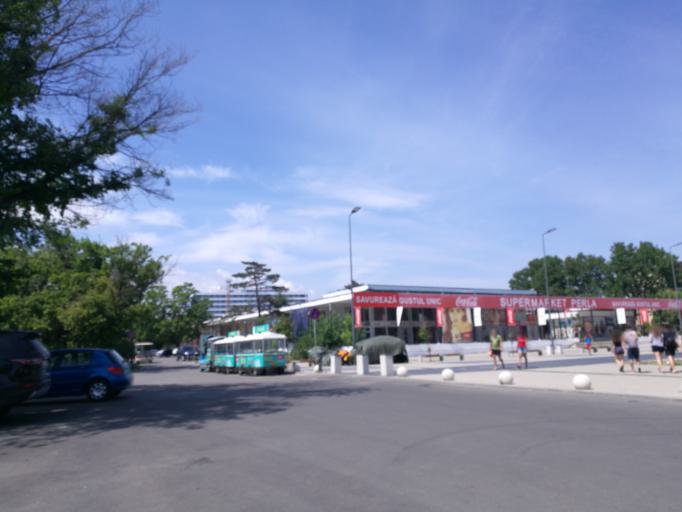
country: RO
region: Constanta
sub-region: Municipiul Constanta
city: Palazu Mare
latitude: 44.2208
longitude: 28.6328
